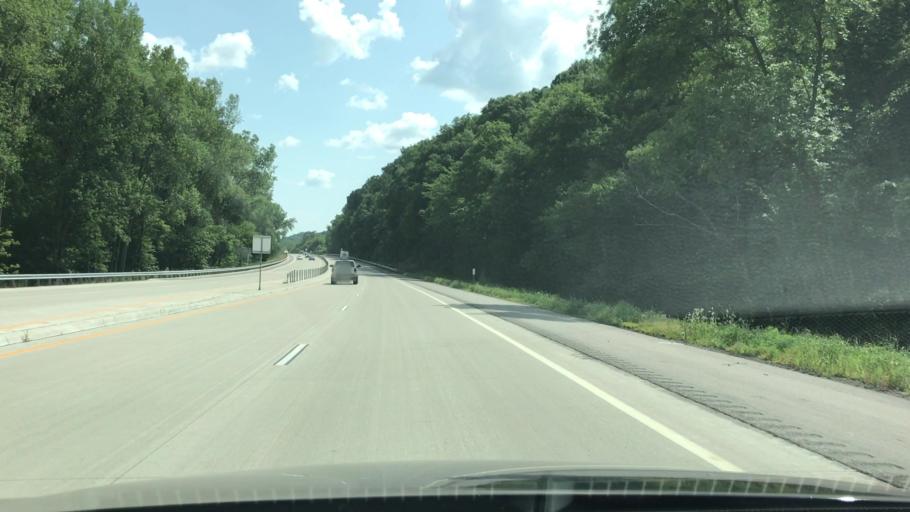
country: US
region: Minnesota
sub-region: Nicollet County
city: North Mankato
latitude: 44.2609
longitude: -94.0270
